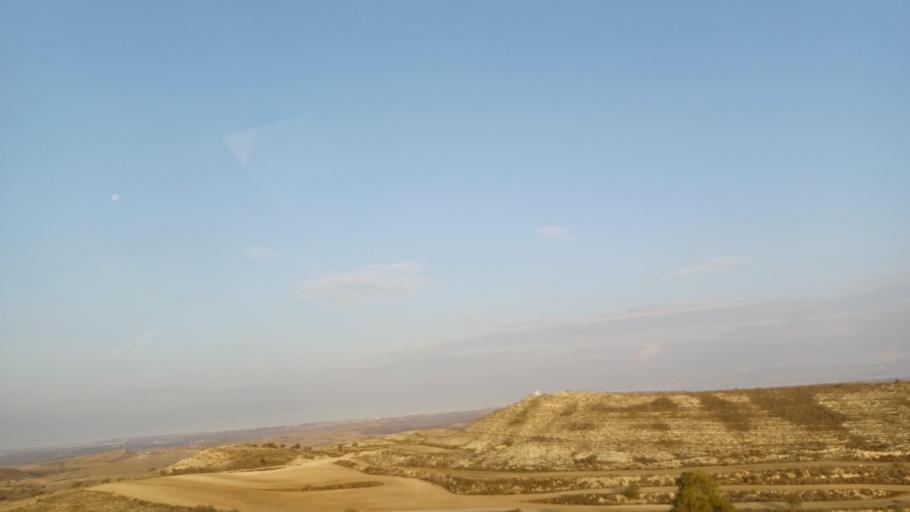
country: CY
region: Larnaka
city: Athienou
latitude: 35.0163
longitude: 33.5369
